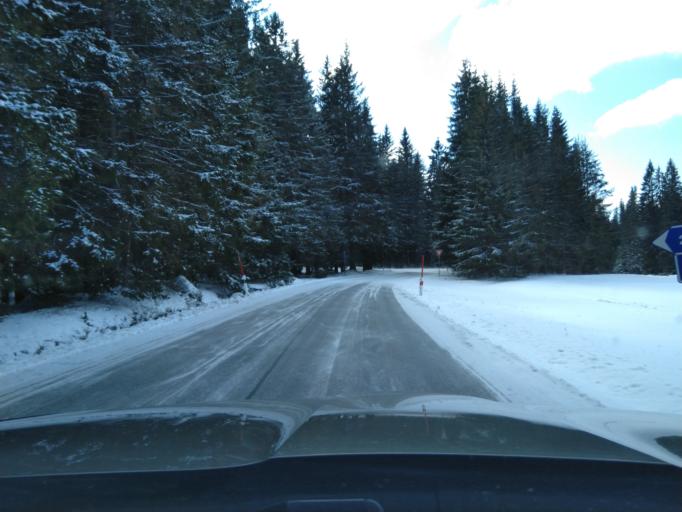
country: CZ
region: Jihocesky
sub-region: Okres Prachatice
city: Borova Lada
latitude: 49.0375
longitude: 13.5784
